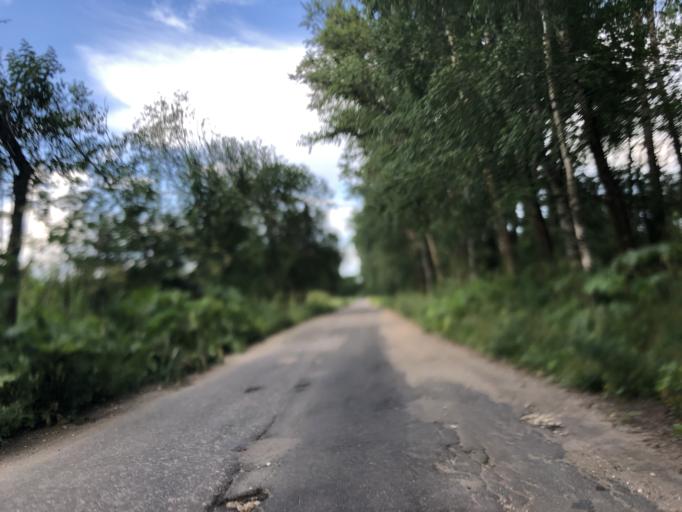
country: RU
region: Tverskaya
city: Rzhev
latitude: 56.2659
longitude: 34.2514
